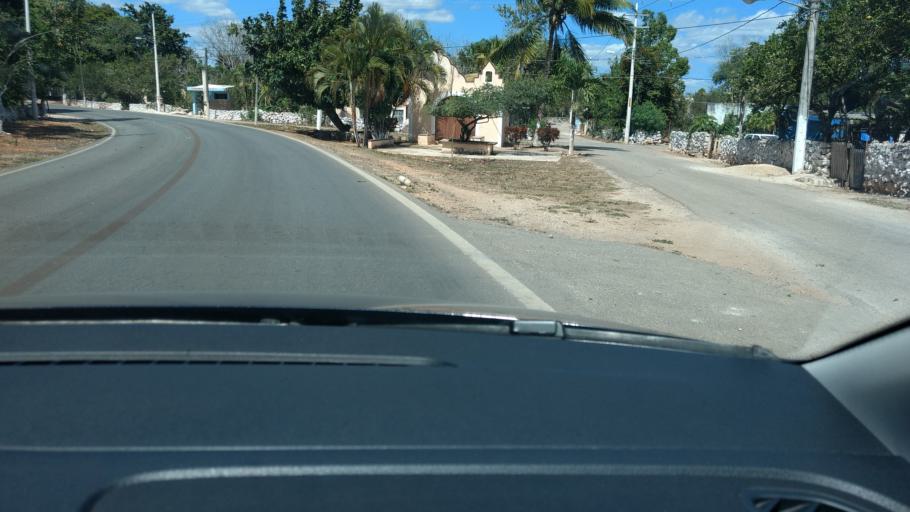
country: MX
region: Yucatan
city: Tzucacab
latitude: 20.0739
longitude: -89.0559
